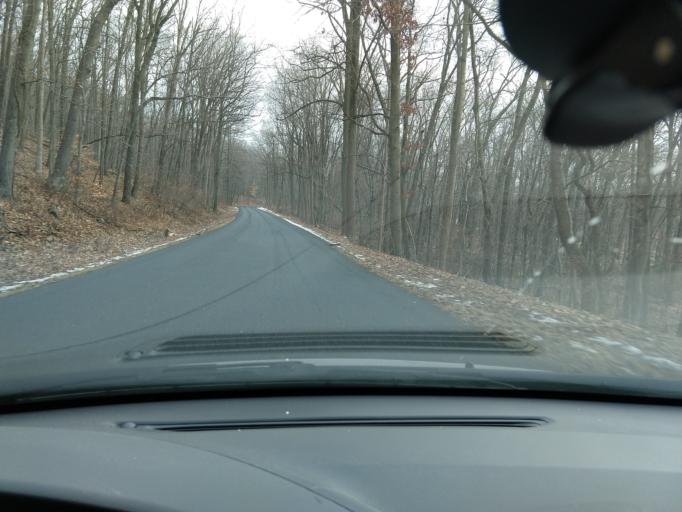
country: US
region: Pennsylvania
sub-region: Chester County
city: Elverson
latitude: 40.1922
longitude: -75.7847
